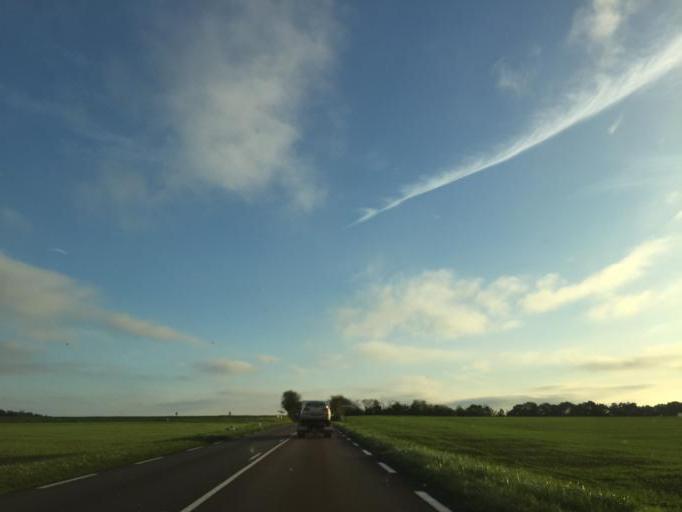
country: FR
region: Ile-de-France
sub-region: Departement de Seine-et-Marne
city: Bray-sur-Seine
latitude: 48.3726
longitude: 3.2335
